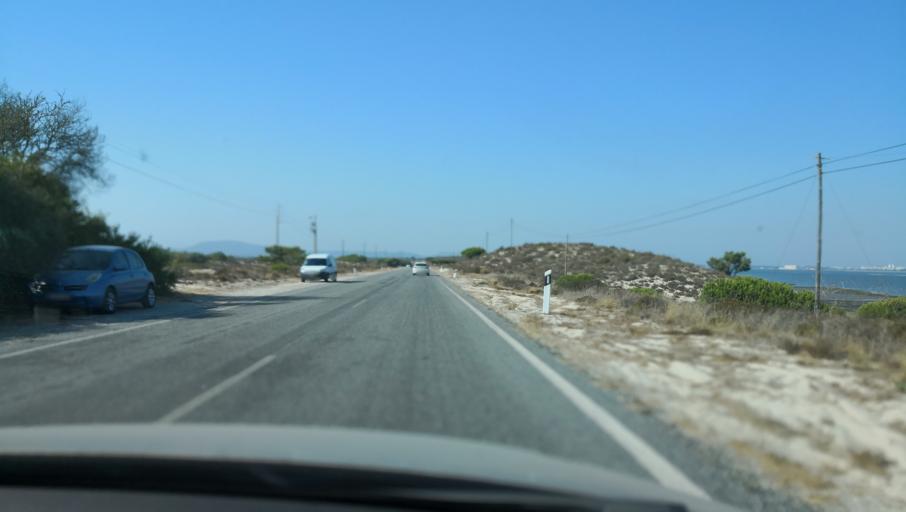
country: PT
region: Setubal
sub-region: Setubal
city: Setubal
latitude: 38.4231
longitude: -8.8222
